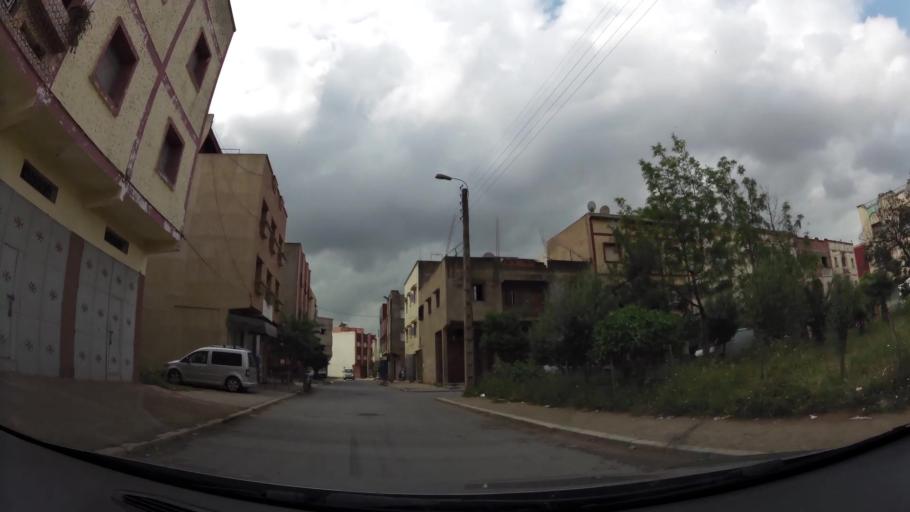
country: MA
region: Rabat-Sale-Zemmour-Zaer
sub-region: Khemisset
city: Tiflet
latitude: 33.8917
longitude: -6.3300
